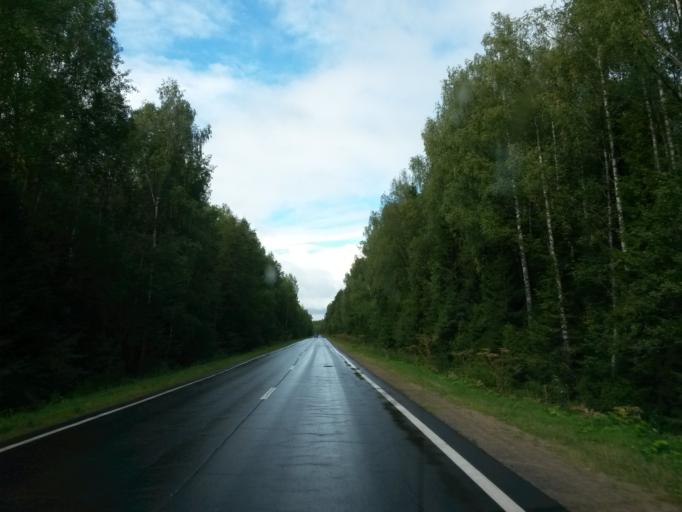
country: RU
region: Jaroslavl
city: Yaroslavl
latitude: 57.8022
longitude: 39.7901
